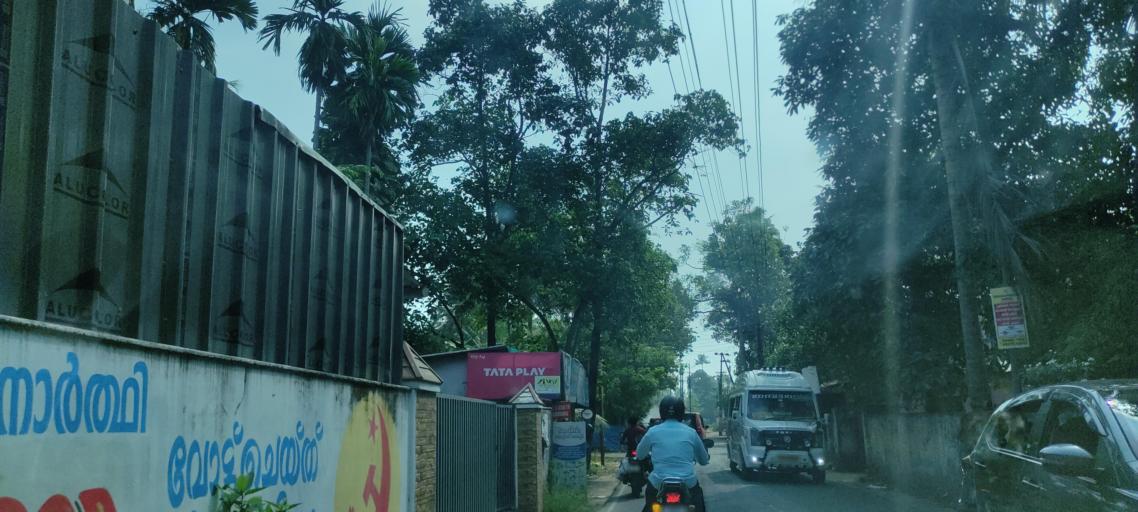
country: IN
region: Kerala
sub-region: Alappuzha
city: Kutiatodu
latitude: 9.8224
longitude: 76.3041
